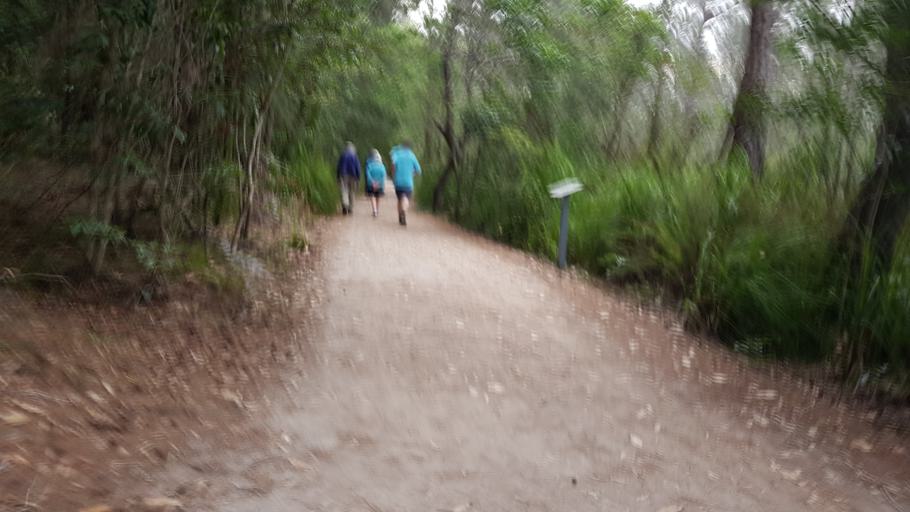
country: AU
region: New South Wales
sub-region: Warringah
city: Narrabeen
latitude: -33.7196
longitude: 151.2787
